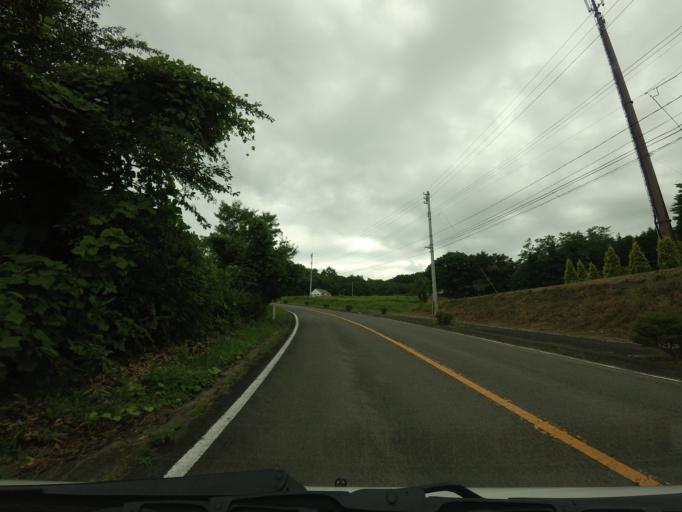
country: JP
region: Fukushima
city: Motomiya
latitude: 37.5783
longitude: 140.3430
